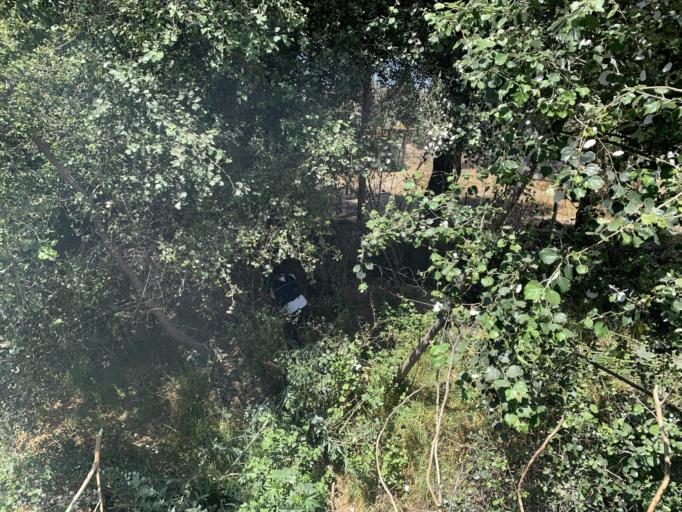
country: MX
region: Puebla
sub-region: Juan C. Bonilla
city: Santa Maria Zacatepec
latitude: 19.1254
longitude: -98.3619
